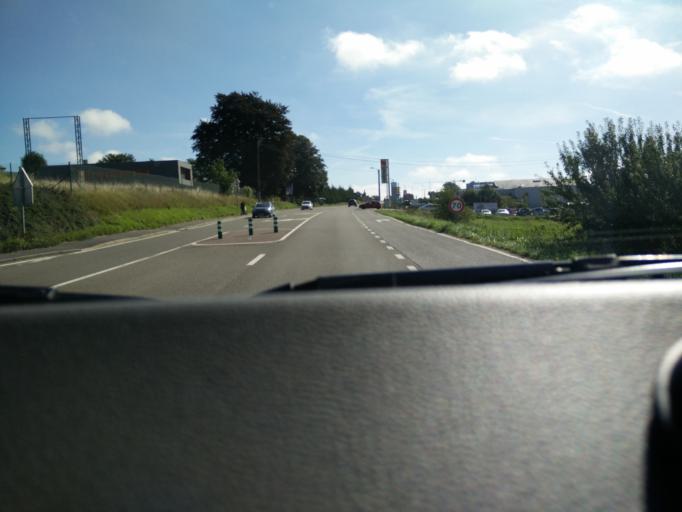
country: BE
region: Wallonia
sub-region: Province de Namur
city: Dinant
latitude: 50.2665
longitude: 4.9361
